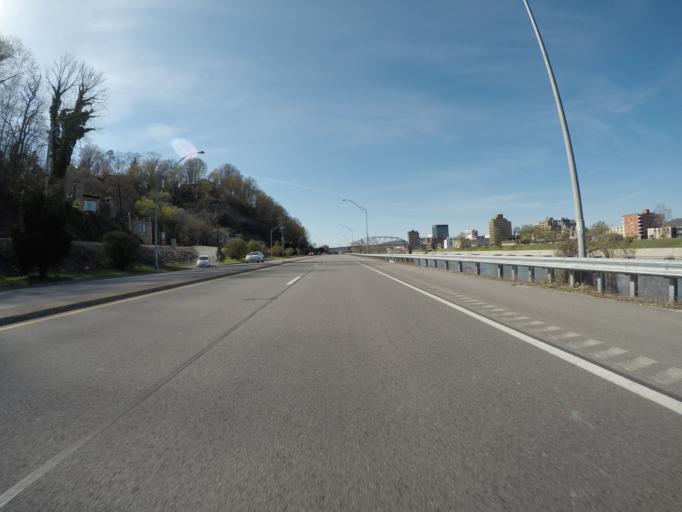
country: US
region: West Virginia
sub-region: Kanawha County
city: Charleston
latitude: 38.3420
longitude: -81.6333
